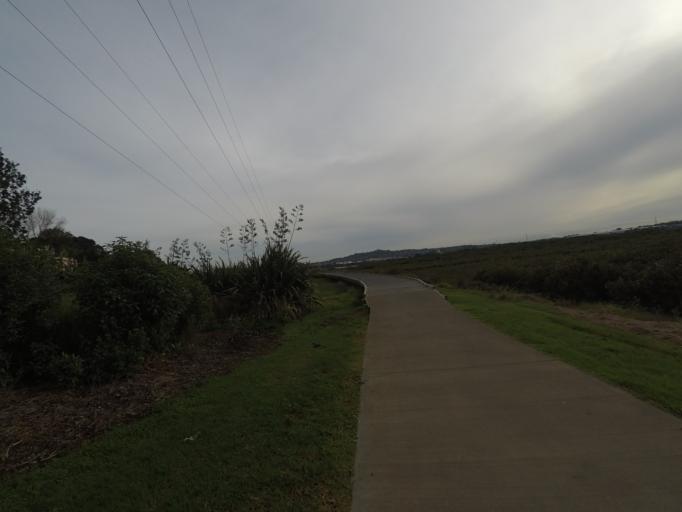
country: NZ
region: Auckland
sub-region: Auckland
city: Mangere
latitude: -36.9436
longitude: 174.7982
